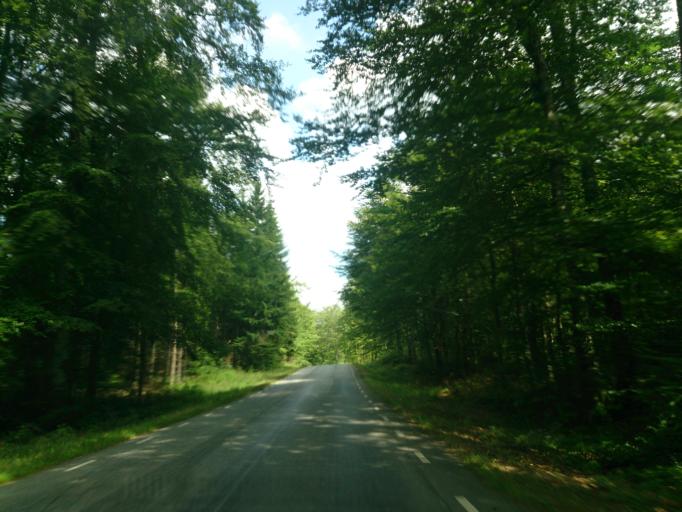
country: SE
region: Joenkoeping
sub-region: Varnamo Kommun
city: Forsheda
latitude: 57.1375
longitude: 13.8740
